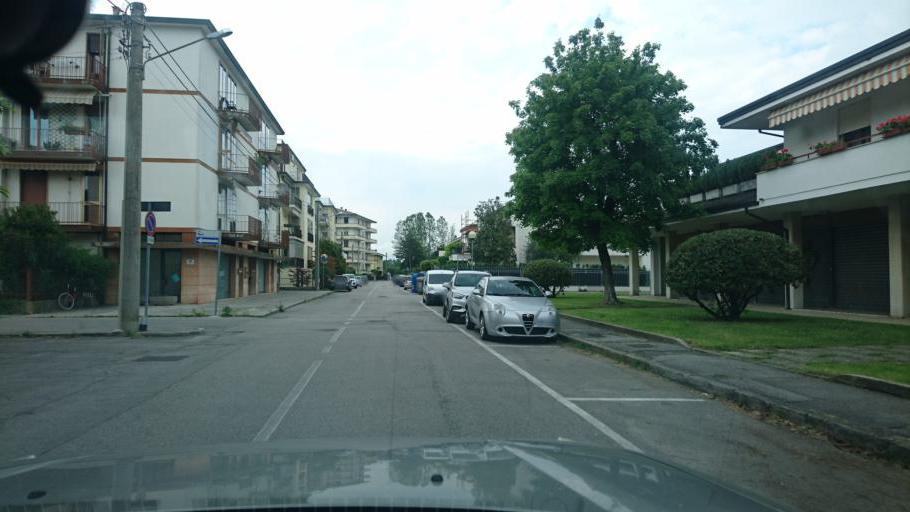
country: IT
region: Veneto
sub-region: Provincia di Padova
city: Mandriola-Sant'Agostino
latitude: 45.3879
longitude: 11.8579
